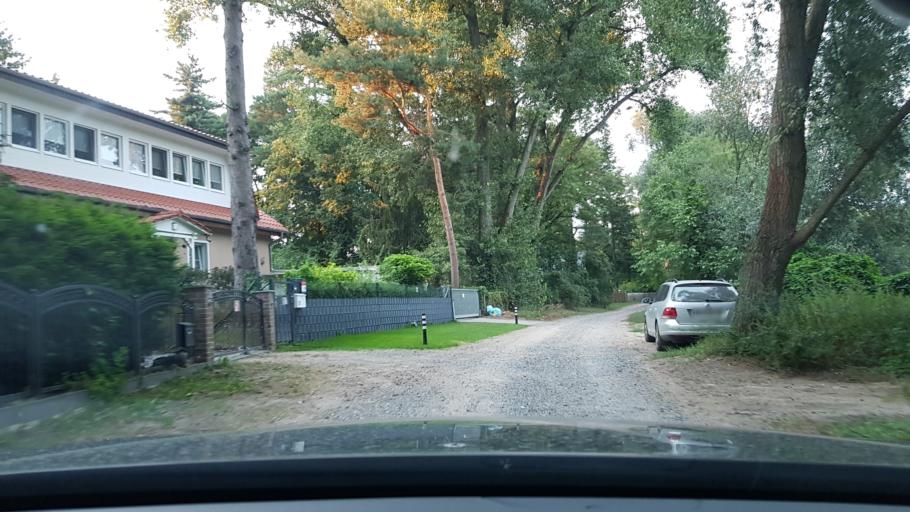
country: DE
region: Berlin
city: Mahlsdorf
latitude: 52.4835
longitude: 13.6299
